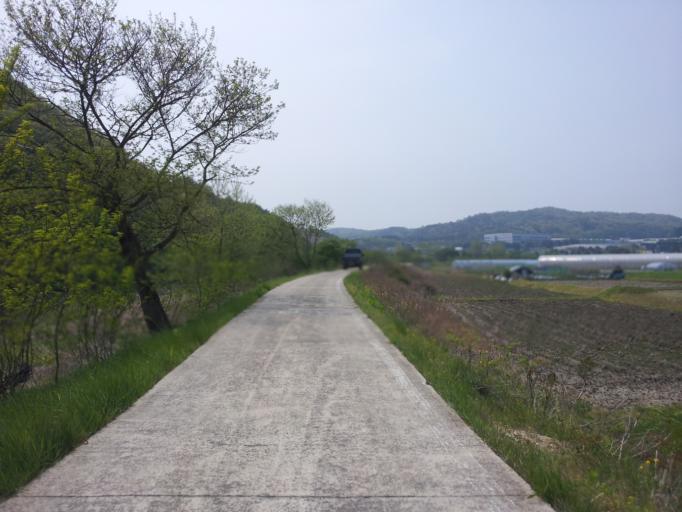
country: KR
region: Daejeon
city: Daejeon
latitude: 36.2570
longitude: 127.2872
